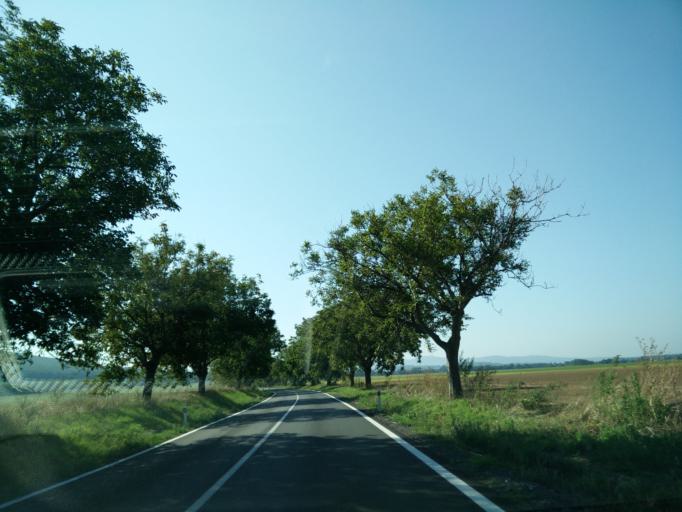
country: SK
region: Nitriansky
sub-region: Okres Nitra
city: Nitra
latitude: 48.4575
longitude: 18.1428
